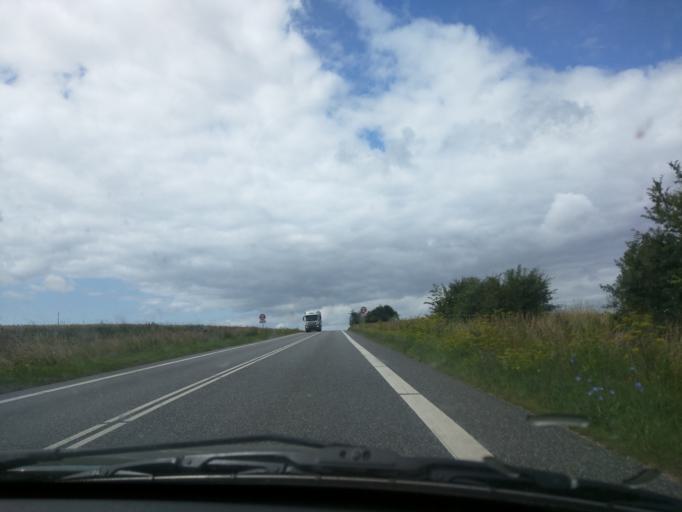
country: DK
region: Zealand
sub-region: Kalundborg Kommune
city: Svebolle
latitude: 55.6743
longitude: 11.1912
